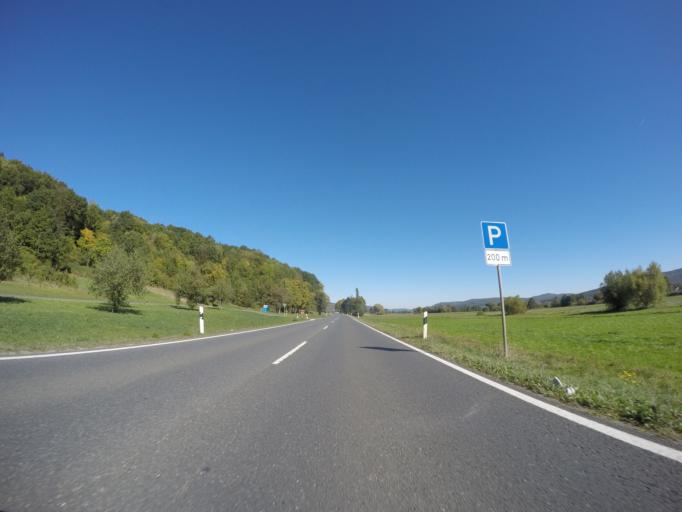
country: DE
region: Bavaria
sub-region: Upper Franconia
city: Wiesenthau
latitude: 49.7327
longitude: 11.1284
